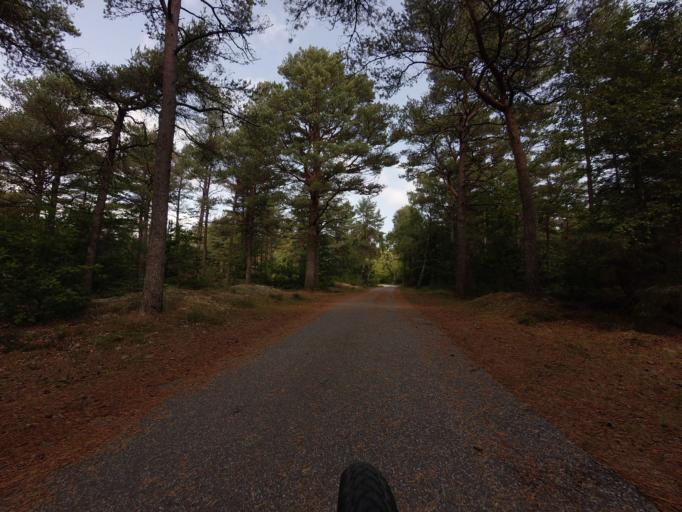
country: DK
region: North Denmark
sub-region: Frederikshavn Kommune
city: Strandby
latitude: 57.6308
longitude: 10.4353
